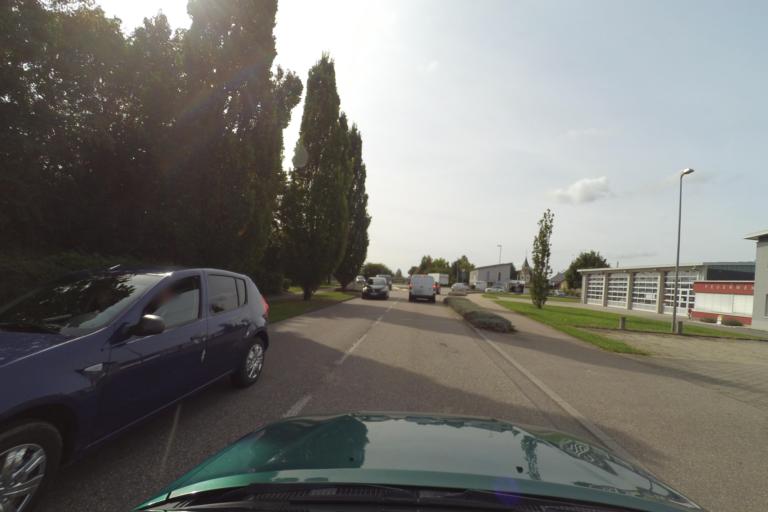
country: DE
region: Baden-Wuerttemberg
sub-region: Freiburg Region
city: Mahlberg
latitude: 48.2847
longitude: 7.8064
